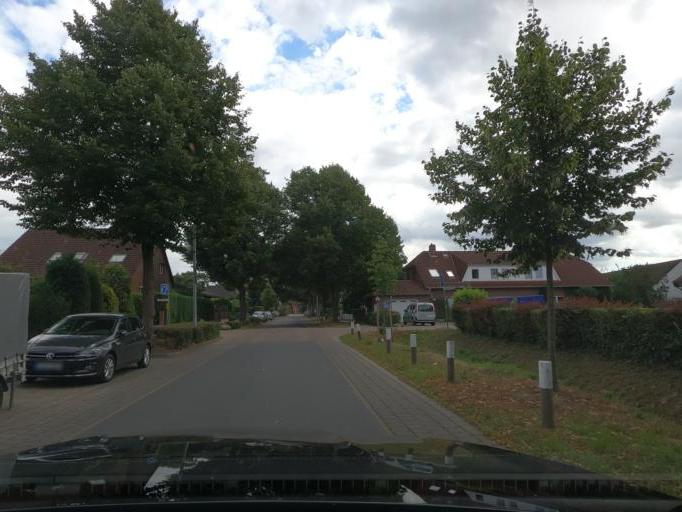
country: DE
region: Lower Saxony
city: Isernhagen Farster Bauerschaft
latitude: 52.4464
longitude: 9.8951
